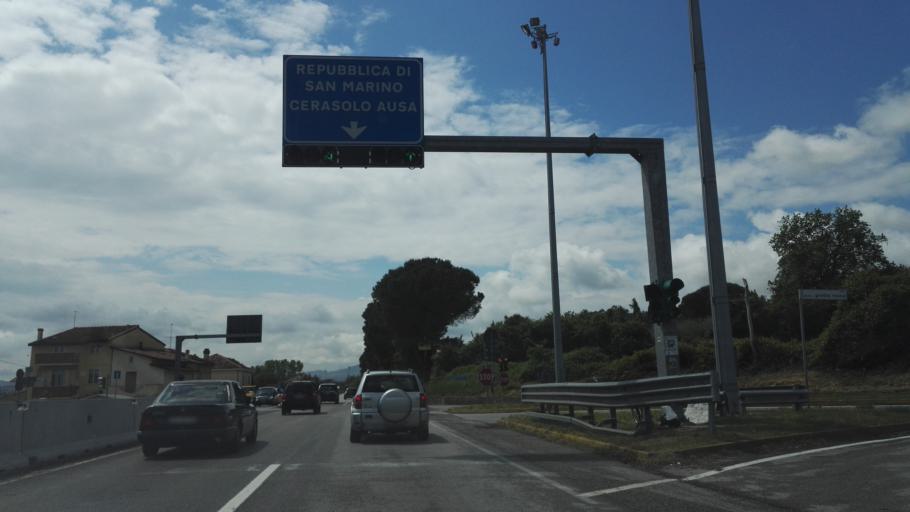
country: IT
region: Emilia-Romagna
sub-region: Provincia di Rimini
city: Rimini
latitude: 44.0254
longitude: 12.5503
